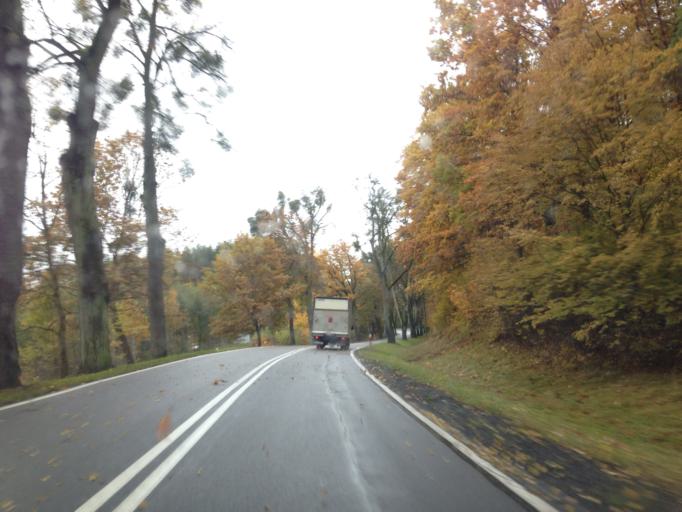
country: PL
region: Pomeranian Voivodeship
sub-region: Powiat kwidzynski
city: Ryjewo
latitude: 53.8584
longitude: 19.0012
